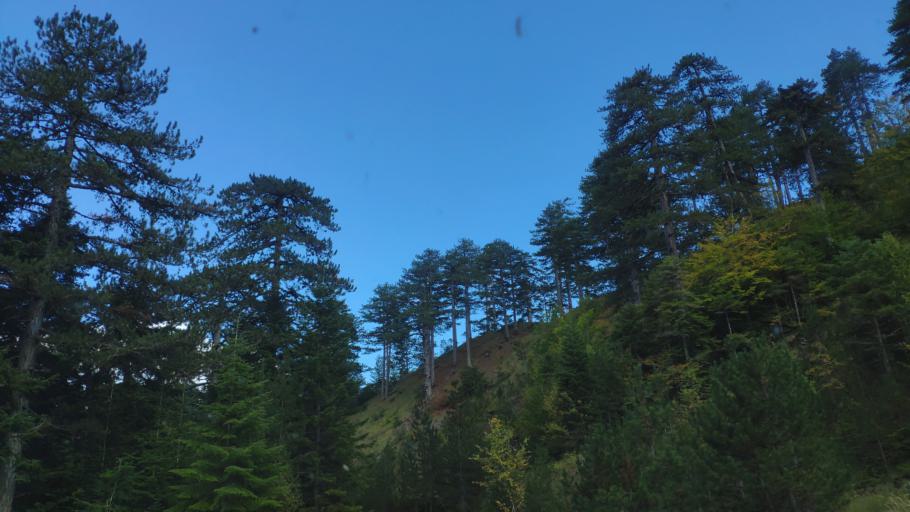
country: AL
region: Korce
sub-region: Rrethi i Devollit
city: Miras
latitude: 40.3371
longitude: 20.8984
